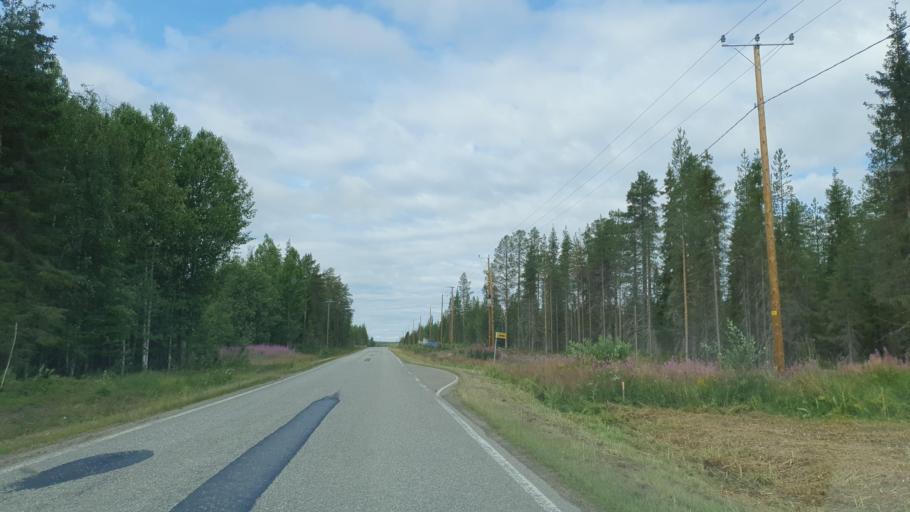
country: FI
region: Lapland
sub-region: Pohjois-Lappi
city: Sodankylae
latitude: 67.4754
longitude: 26.1320
